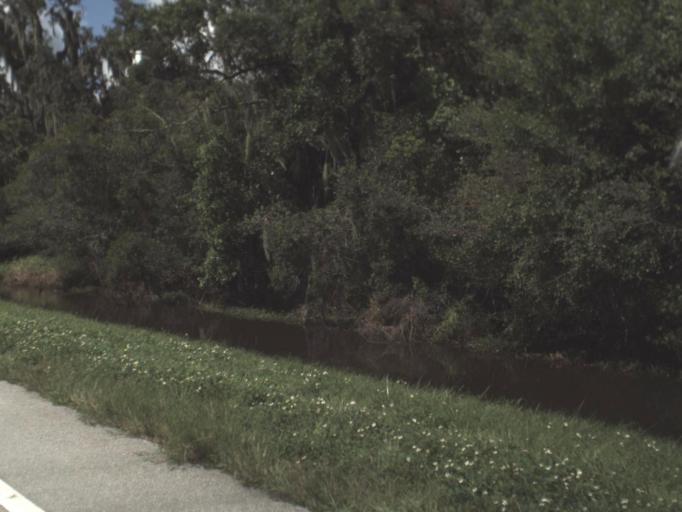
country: US
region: Florida
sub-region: DeSoto County
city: Arcadia
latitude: 27.2910
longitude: -82.0536
